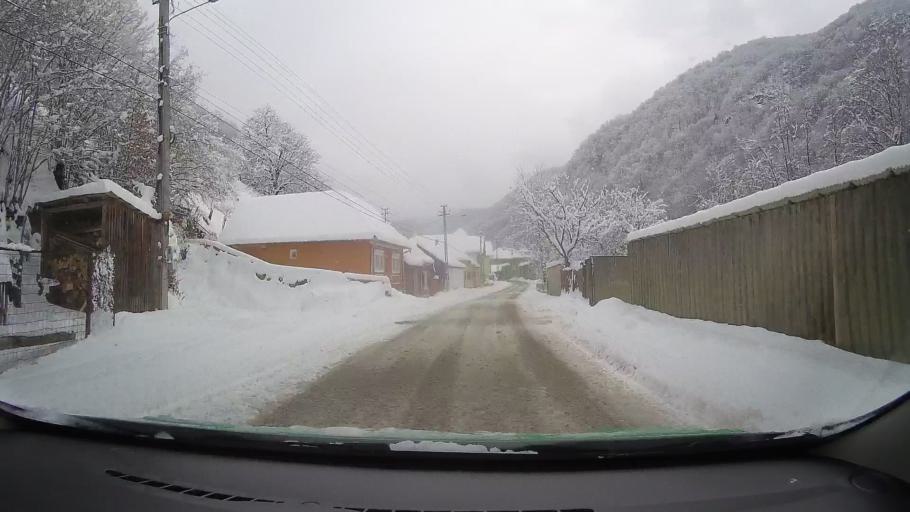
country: RO
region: Alba
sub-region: Comuna Sugag
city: Dobra
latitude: 45.7609
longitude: 23.6603
